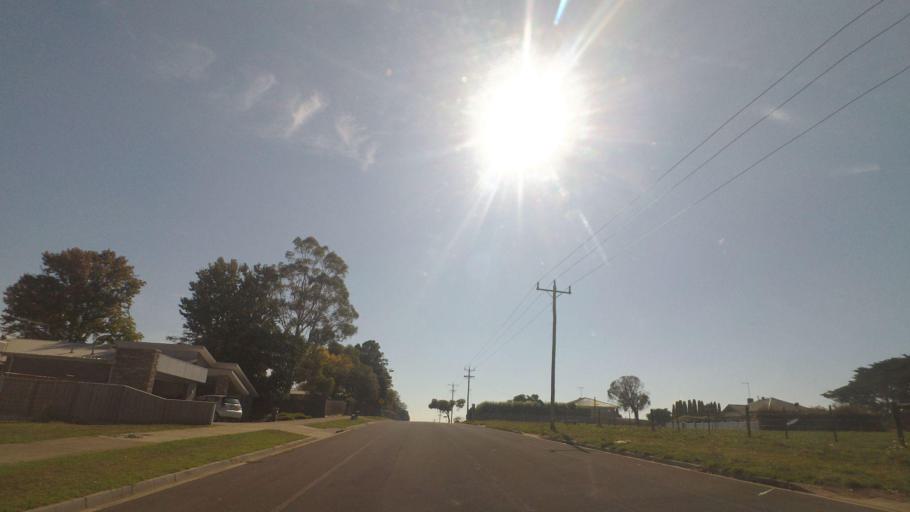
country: AU
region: Victoria
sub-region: Baw Baw
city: Warragul
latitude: -38.1497
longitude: 145.9419
